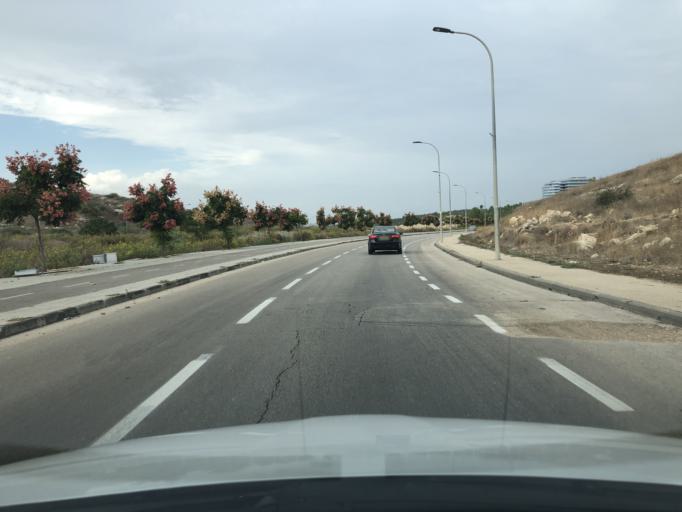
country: PS
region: West Bank
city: Al Midyah
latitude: 31.9189
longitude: 34.9979
